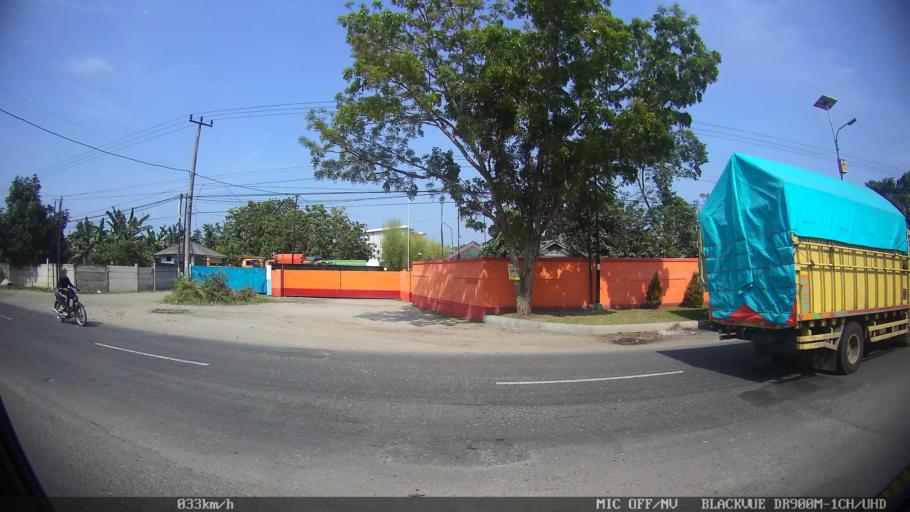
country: ID
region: Lampung
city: Natar
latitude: -5.2652
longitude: 105.1861
